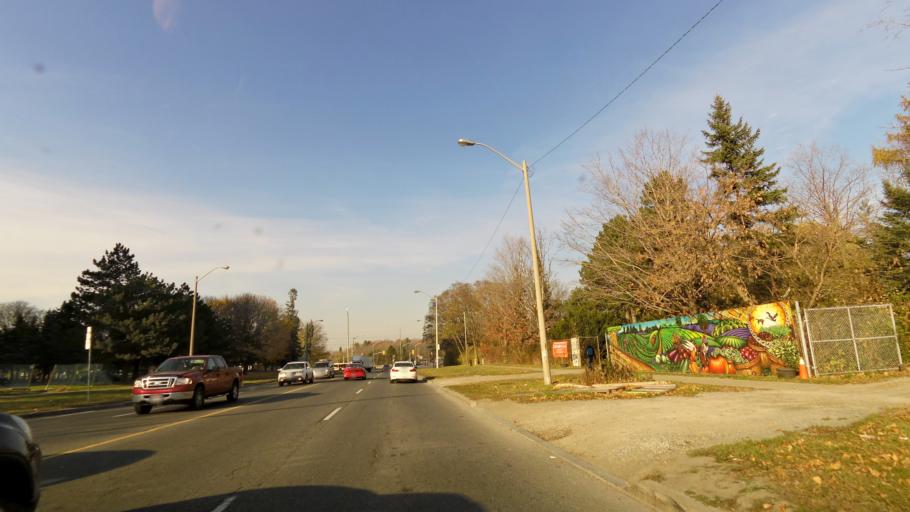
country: CA
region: Ontario
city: Concord
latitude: 43.7735
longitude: -79.5214
